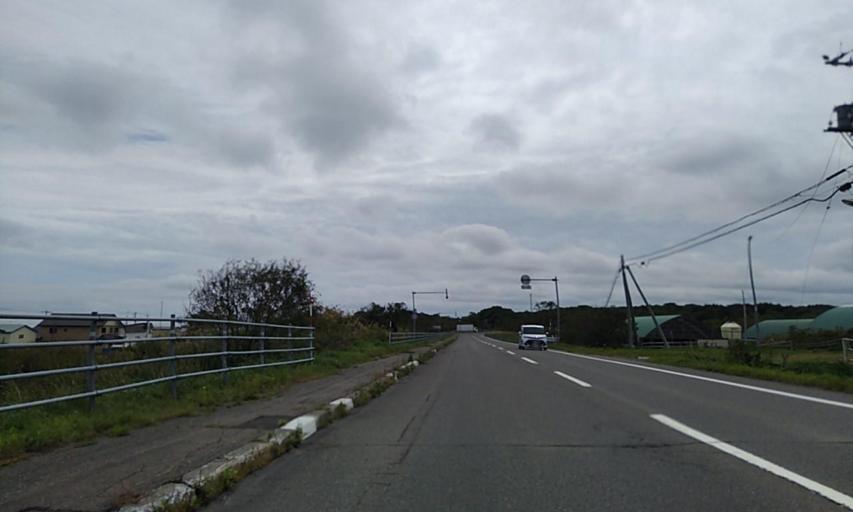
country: JP
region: Hokkaido
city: Shibetsu
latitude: 43.5514
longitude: 145.2257
